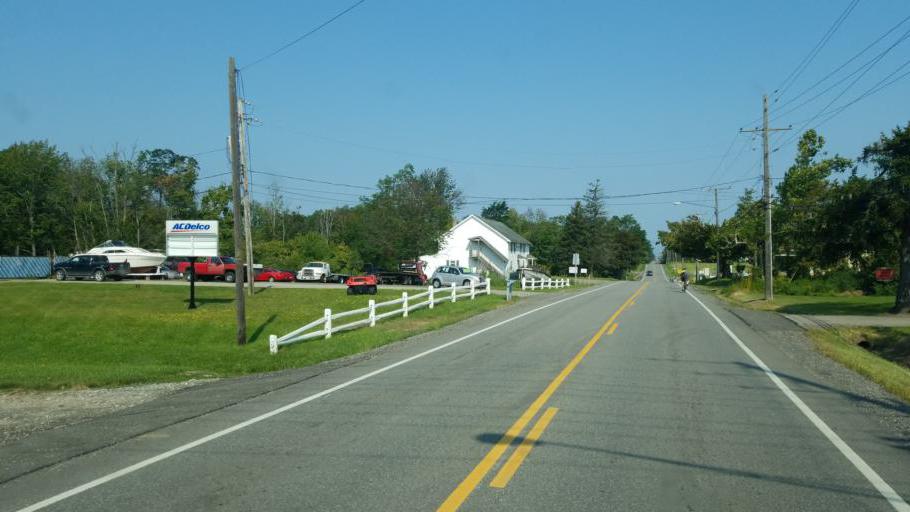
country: US
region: Ohio
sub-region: Geauga County
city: Chardon
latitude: 41.6049
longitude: -81.1470
